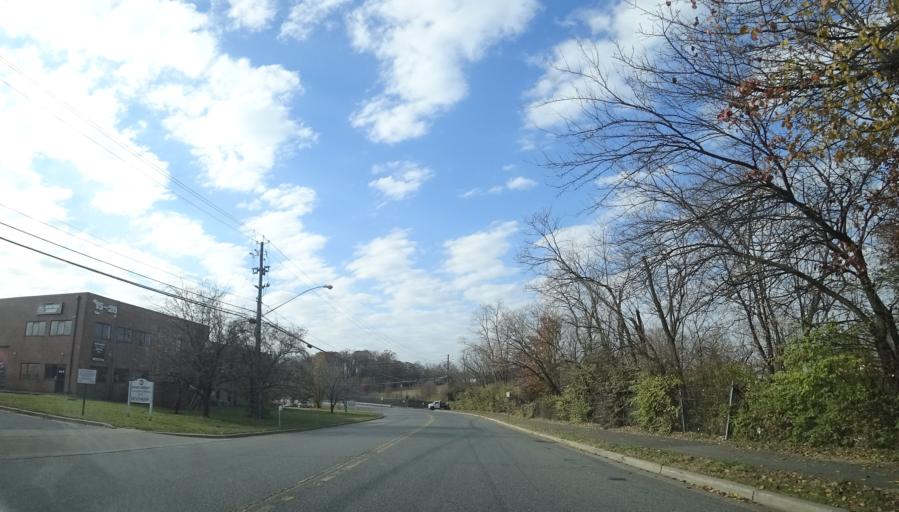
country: US
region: Maryland
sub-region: Montgomery County
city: Rockville
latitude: 39.0987
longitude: -77.1412
